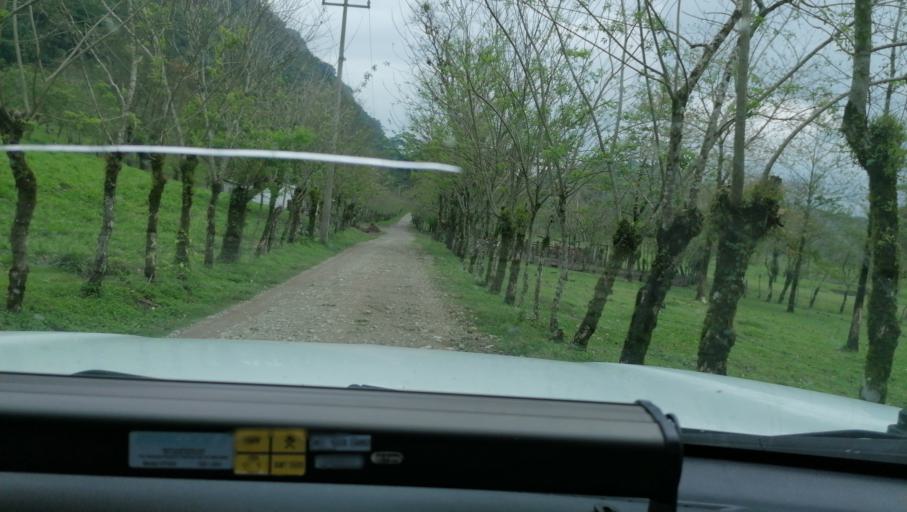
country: MX
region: Chiapas
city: Ixtacomitan
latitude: 17.3510
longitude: -93.1564
